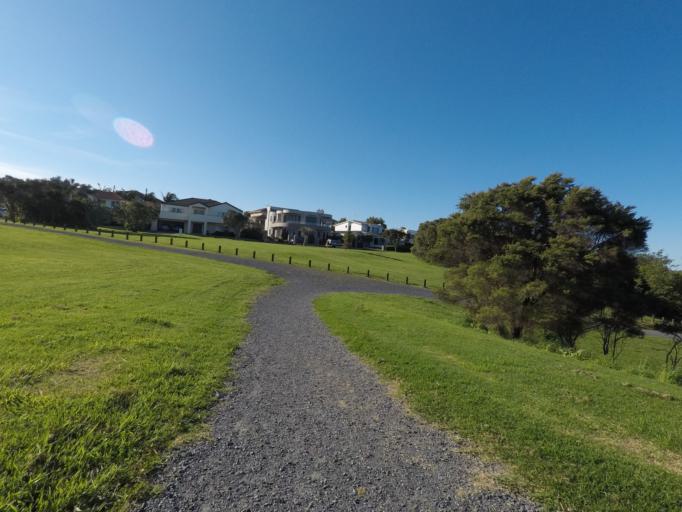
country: NZ
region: Auckland
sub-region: Auckland
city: Rosebank
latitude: -36.8481
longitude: 174.6539
